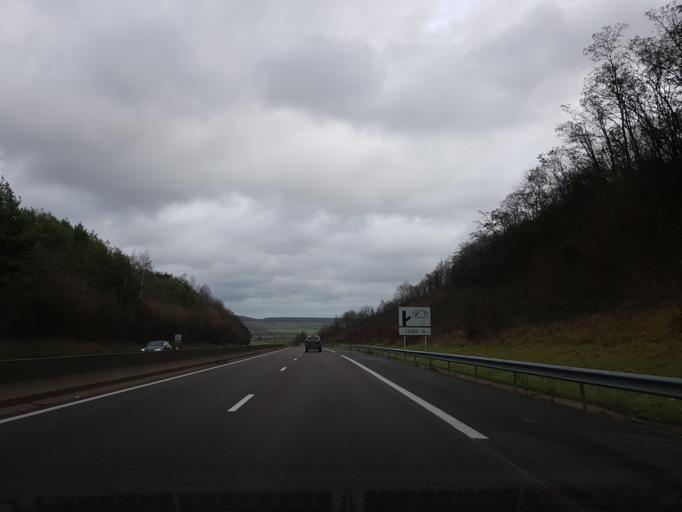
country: FR
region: Champagne-Ardenne
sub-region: Departement de la Haute-Marne
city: Rolampont
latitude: 47.9204
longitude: 5.2601
